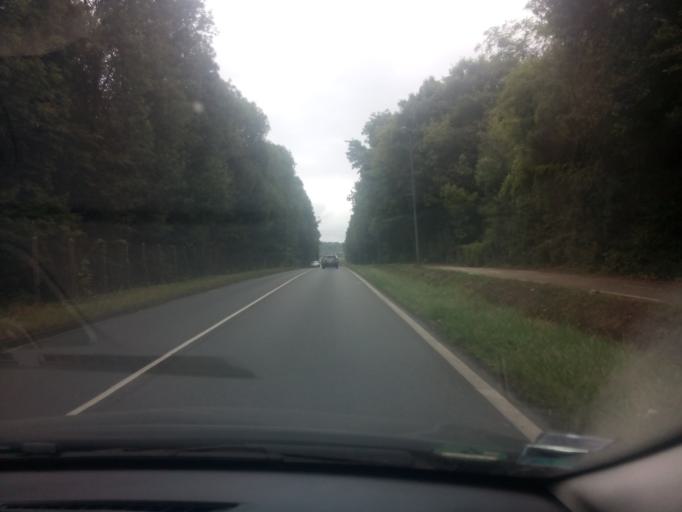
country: FR
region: Ile-de-France
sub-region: Departement de l'Essonne
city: Saulx-les-Chartreux
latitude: 48.7008
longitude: 2.2632
